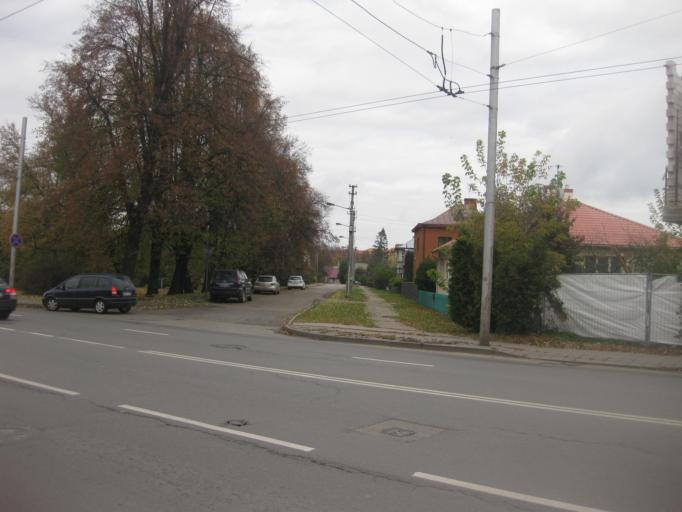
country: LT
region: Kauno apskritis
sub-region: Kaunas
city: Eiguliai
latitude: 54.9100
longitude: 23.9269
